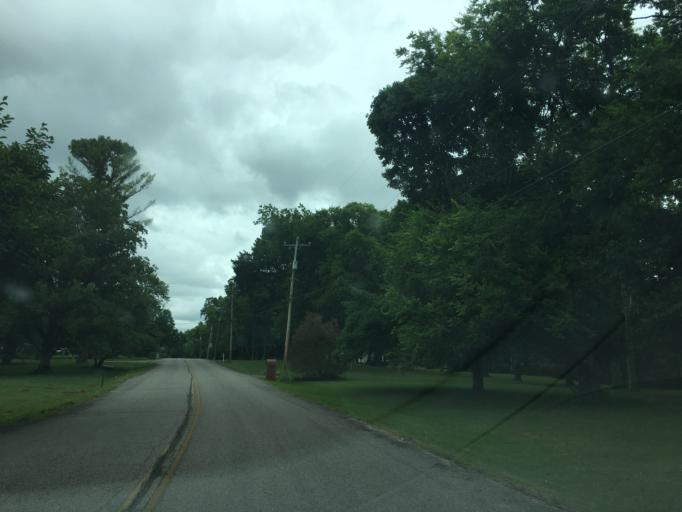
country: US
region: Tennessee
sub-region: Davidson County
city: Oak Hill
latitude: 36.0984
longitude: -86.7838
